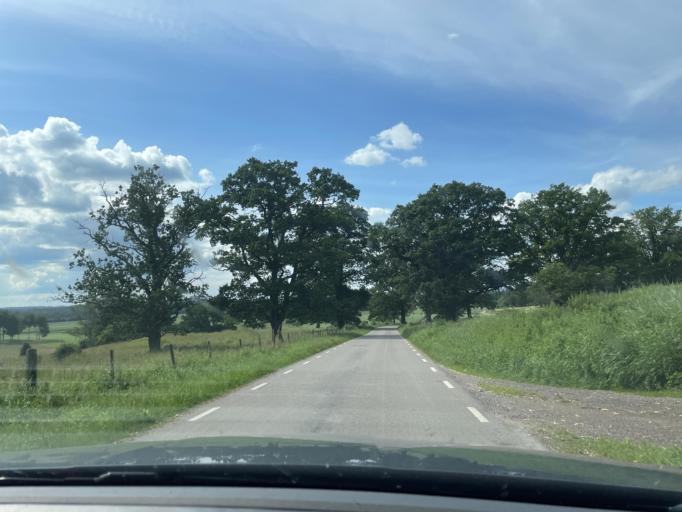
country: SE
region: Kalmar
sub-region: Vimmerby Kommun
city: Sodra Vi
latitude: 57.8059
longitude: 15.7819
